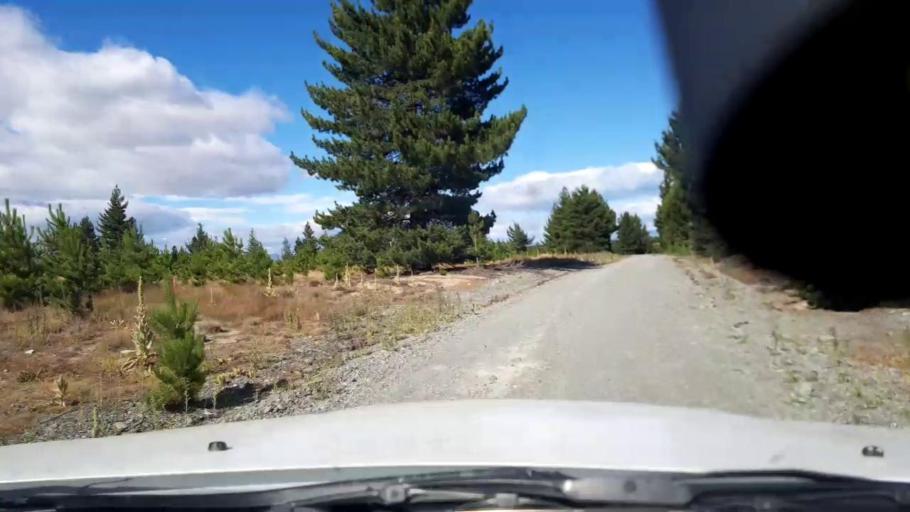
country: NZ
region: Canterbury
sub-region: Timaru District
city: Pleasant Point
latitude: -44.0141
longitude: 170.4733
